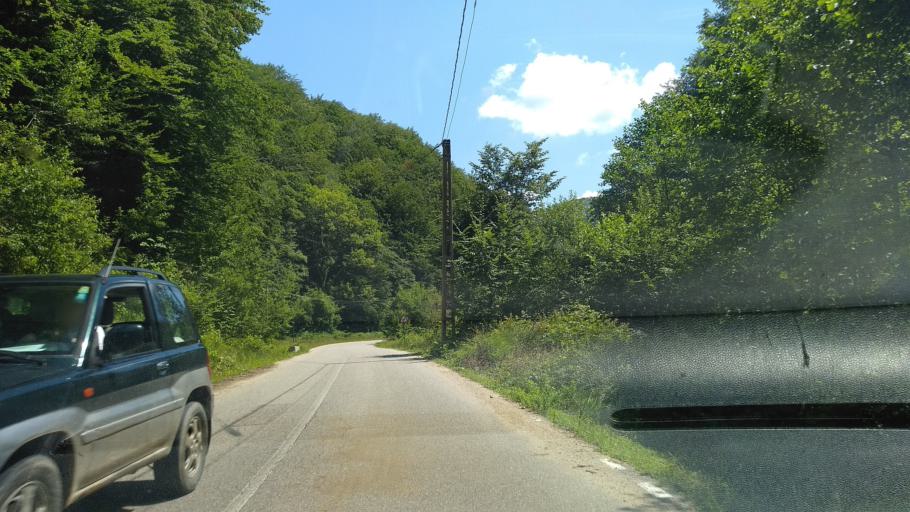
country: RO
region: Hunedoara
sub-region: Comuna Orastioara de Sus
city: Orastioara de Sus
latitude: 45.6301
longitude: 23.2169
